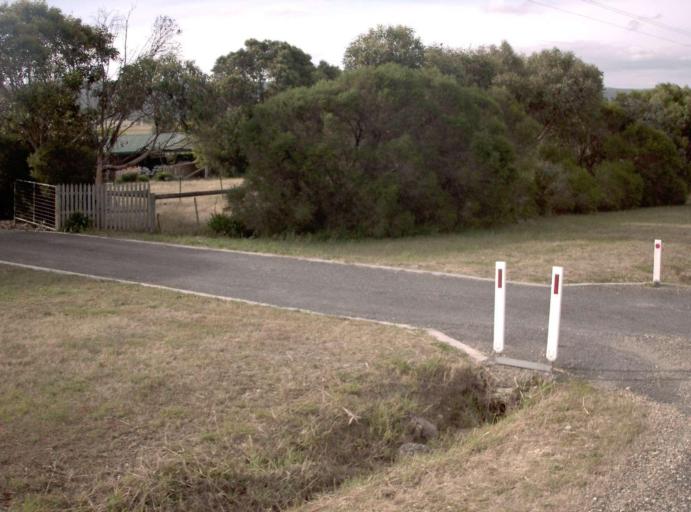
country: AU
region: Victoria
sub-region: Wellington
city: Heyfield
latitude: -38.0228
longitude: 146.6695
